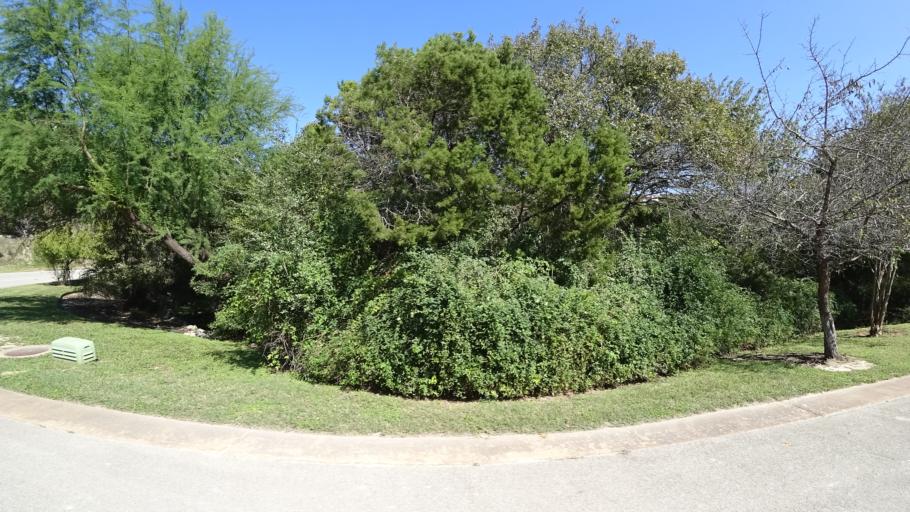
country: US
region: Texas
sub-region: Travis County
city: West Lake Hills
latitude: 30.2969
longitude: -97.8037
